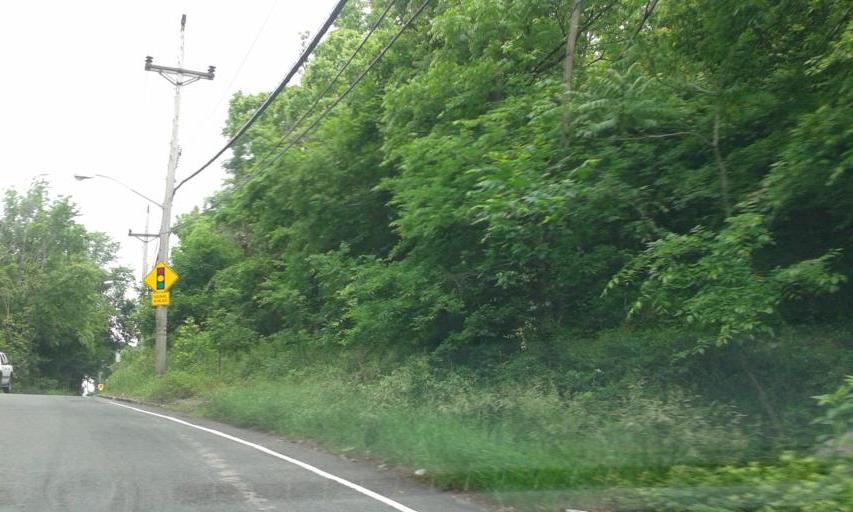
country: US
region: New York
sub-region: Richmond County
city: Staten Island
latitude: 40.5742
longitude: -74.1469
